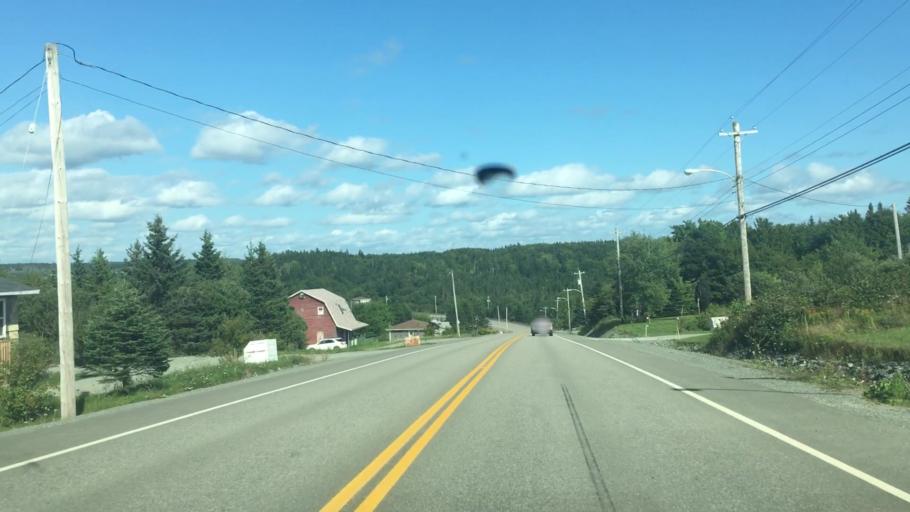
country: CA
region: Nova Scotia
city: Princeville
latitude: 45.6842
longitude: -60.7611
